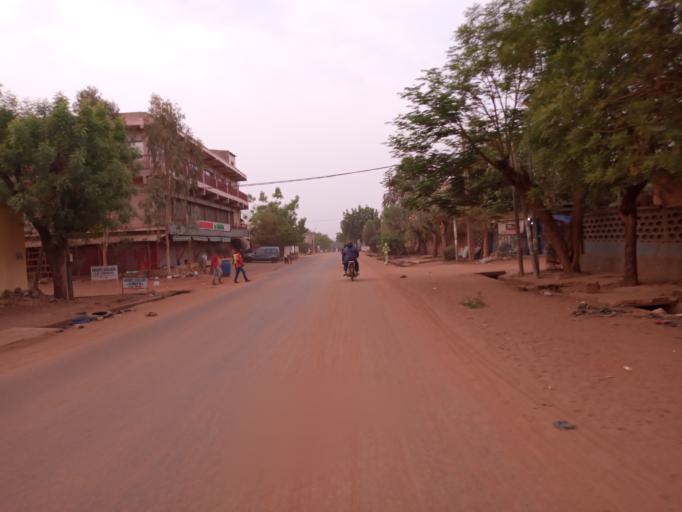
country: ML
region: Bamako
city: Bamako
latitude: 12.6647
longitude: -7.9735
